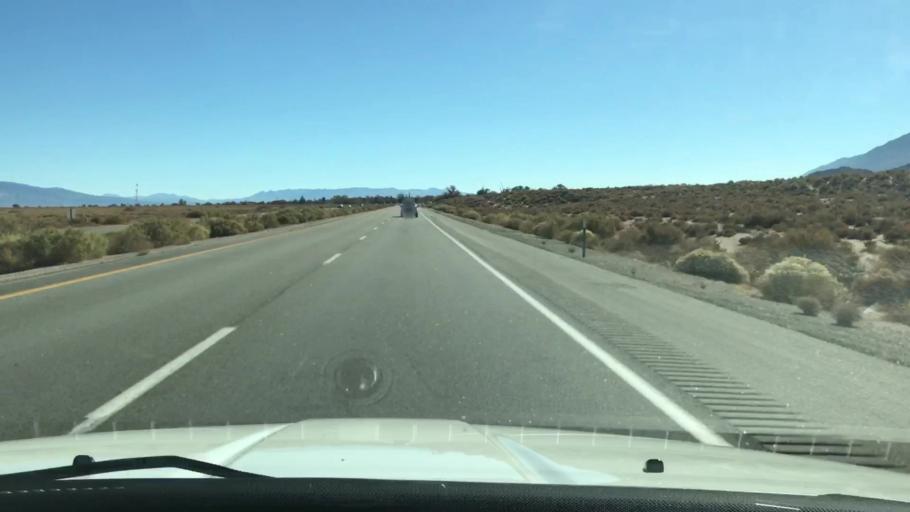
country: US
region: California
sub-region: Inyo County
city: Lone Pine
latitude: 36.6299
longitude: -118.0750
